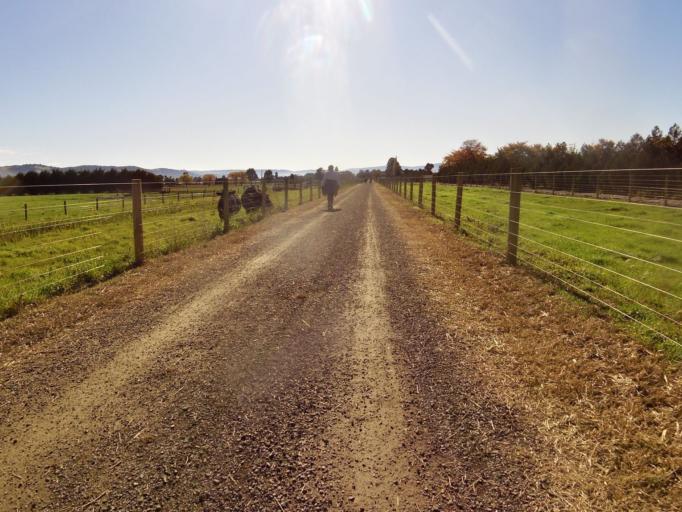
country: AU
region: Victoria
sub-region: Yarra Ranges
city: Yarra Glen
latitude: -37.7040
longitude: 145.3707
